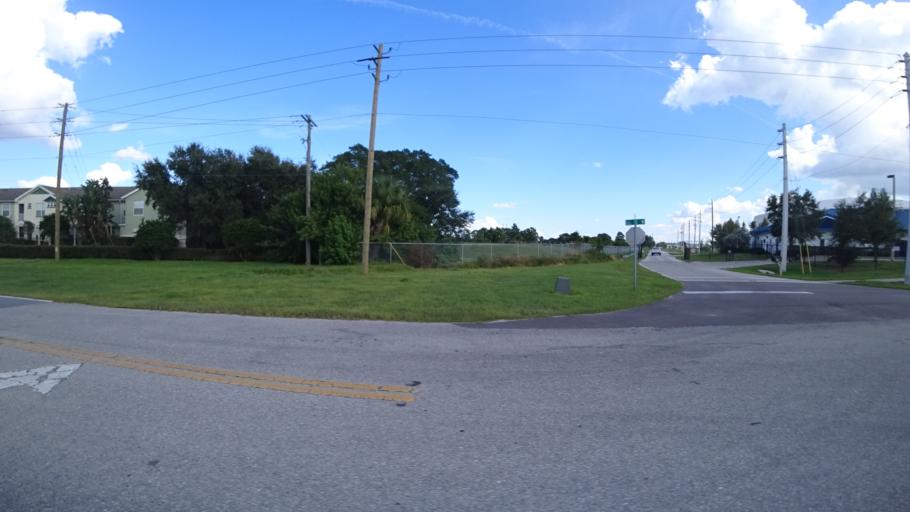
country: US
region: Florida
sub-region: Manatee County
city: South Bradenton
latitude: 27.4572
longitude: -82.6269
